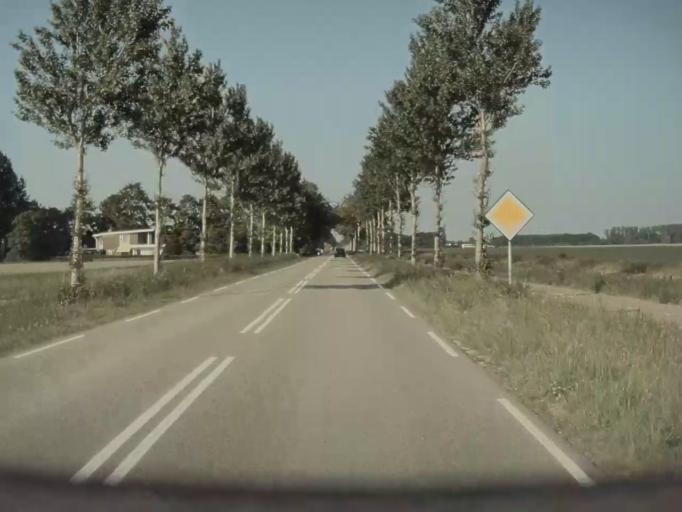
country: NL
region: Zeeland
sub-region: Gemeente Goes
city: Goes
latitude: 51.5877
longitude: 3.8296
